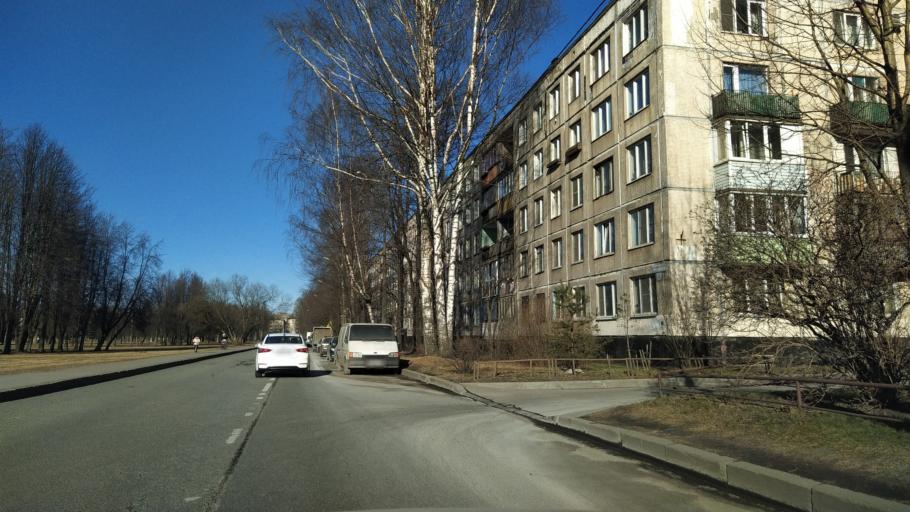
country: RU
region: Leningrad
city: Kalininskiy
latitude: 59.9947
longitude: 30.4287
